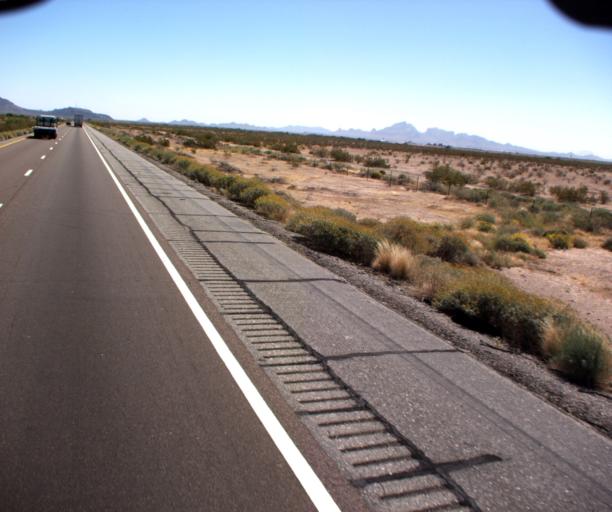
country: US
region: Arizona
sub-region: La Paz County
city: Salome
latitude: 33.5438
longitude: -113.1890
